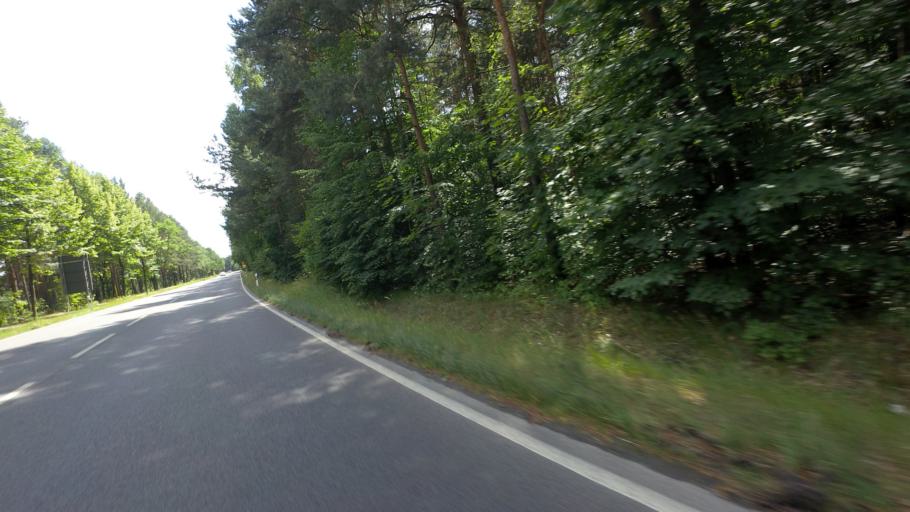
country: DE
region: Brandenburg
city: Senftenberg
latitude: 51.4916
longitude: 14.0690
